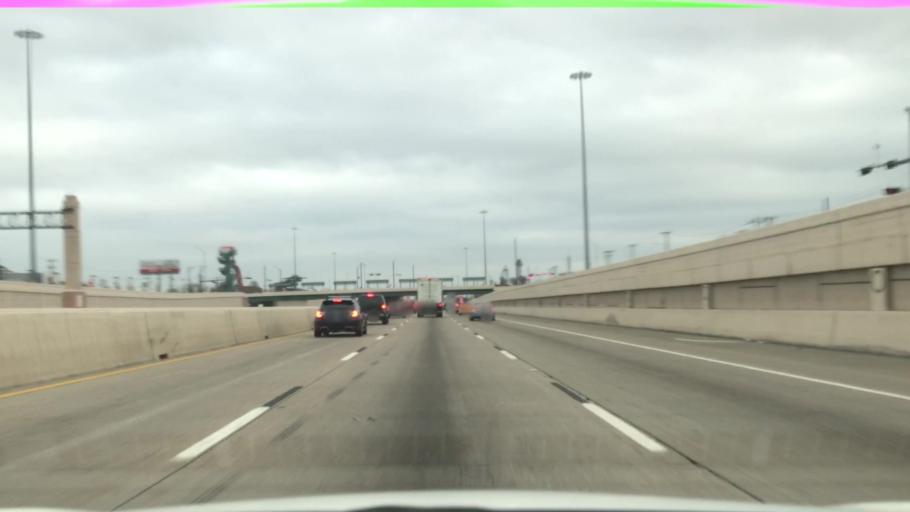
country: US
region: Texas
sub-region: Tarrant County
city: Arlington
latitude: 32.7595
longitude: -97.0893
